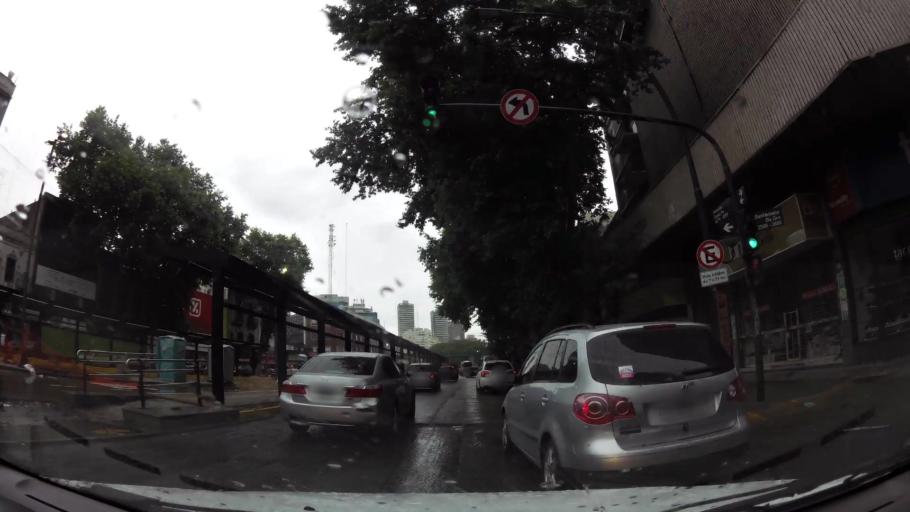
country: AR
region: Buenos Aires F.D.
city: Colegiales
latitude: -34.5791
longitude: -58.4243
